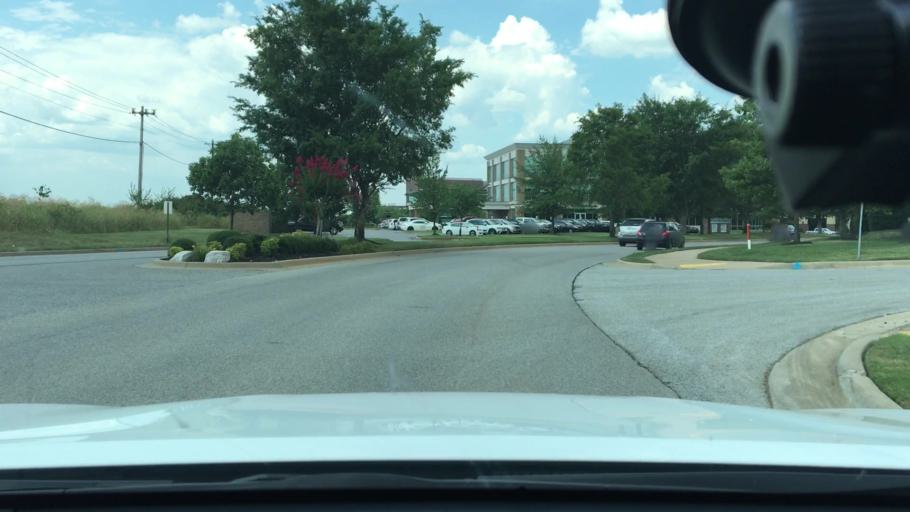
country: US
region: Arkansas
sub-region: Benton County
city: Cave Springs
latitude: 36.3033
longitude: -94.1892
